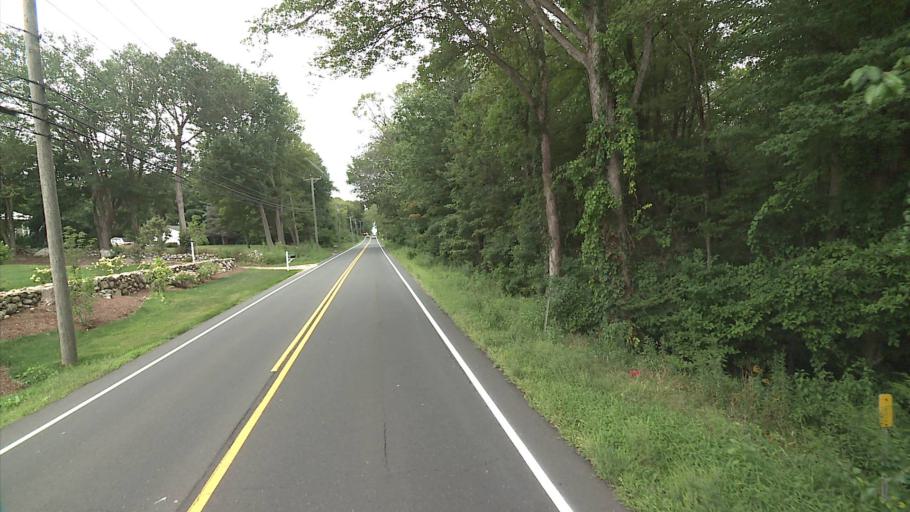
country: US
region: Connecticut
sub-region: New London County
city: Colchester
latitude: 41.5488
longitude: -72.3101
